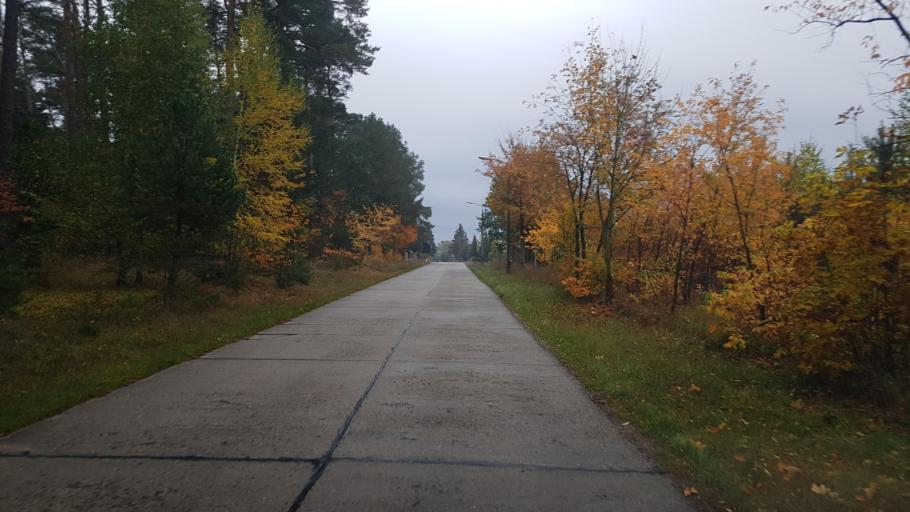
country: DE
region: Brandenburg
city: Schlieben
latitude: 51.7396
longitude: 13.3798
